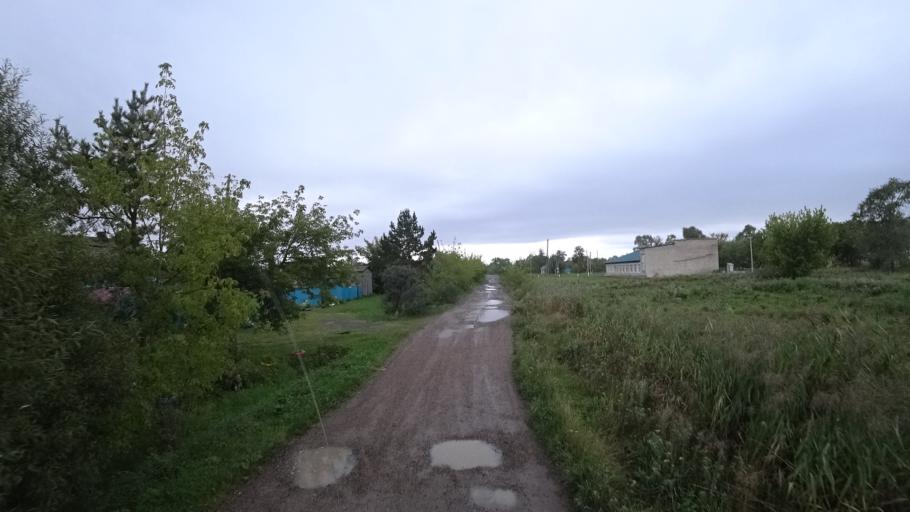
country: RU
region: Primorskiy
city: Chernigovka
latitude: 44.4063
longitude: 132.5320
